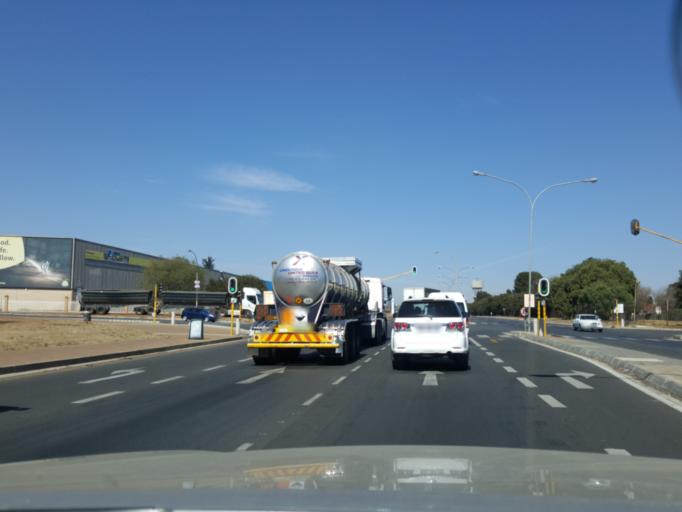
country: ZA
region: Gauteng
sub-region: City of Johannesburg Metropolitan Municipality
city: Modderfontein
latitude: -26.1153
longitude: 28.1990
